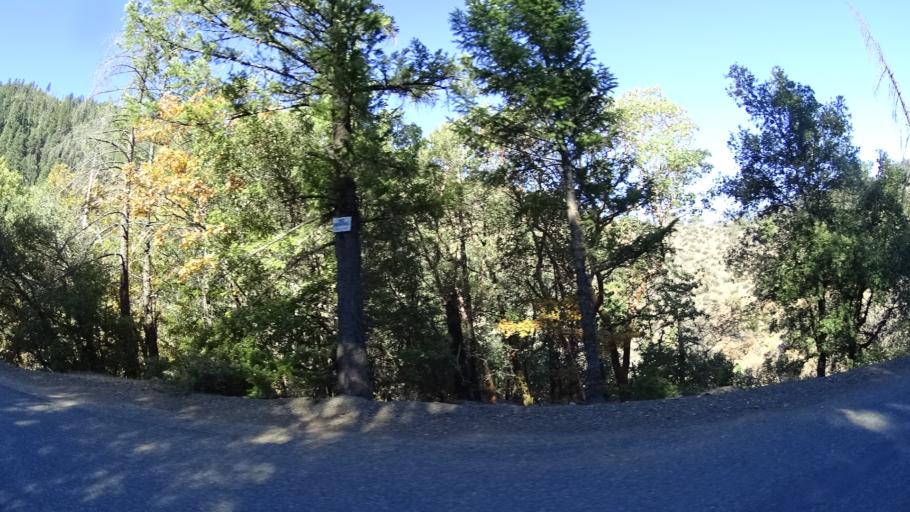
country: US
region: California
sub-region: Humboldt County
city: Willow Creek
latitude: 41.1849
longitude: -123.2179
